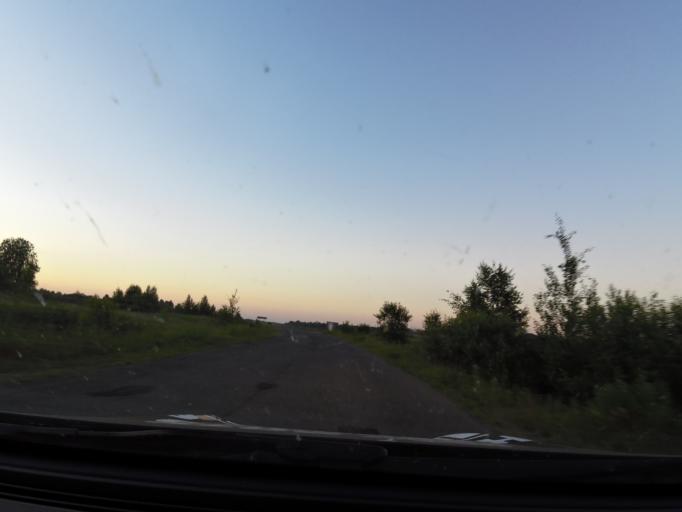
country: RU
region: Kostroma
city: Buy
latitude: 58.3581
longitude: 41.2018
